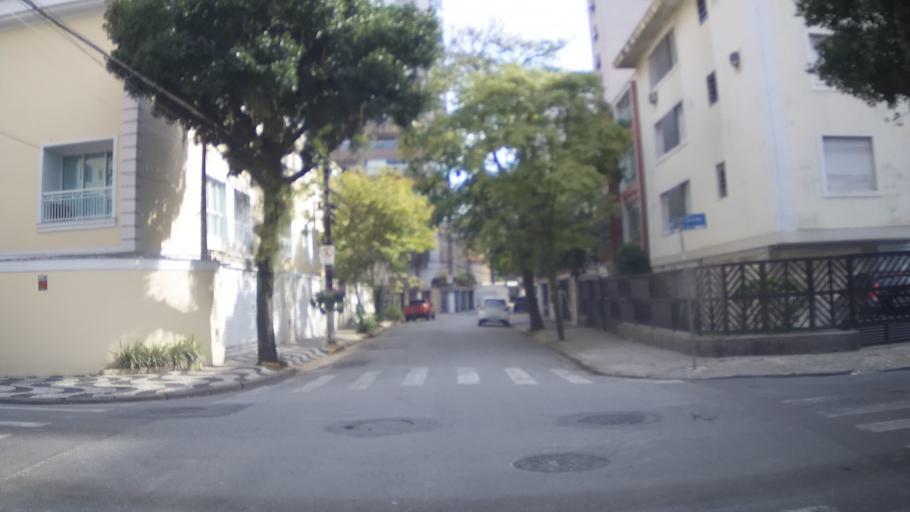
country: BR
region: Sao Paulo
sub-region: Santos
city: Santos
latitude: -23.9634
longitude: -46.3297
